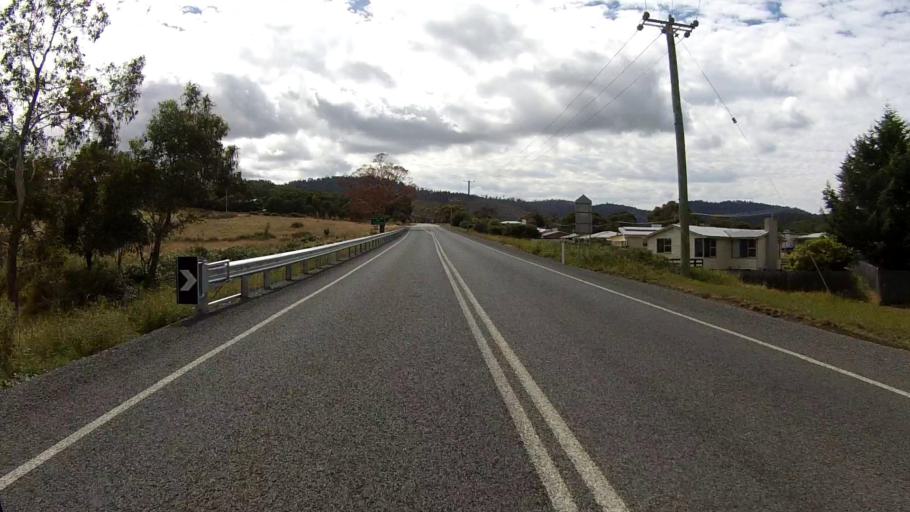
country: AU
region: Tasmania
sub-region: Clarence
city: Lindisfarne
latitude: -42.8081
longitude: 147.3467
